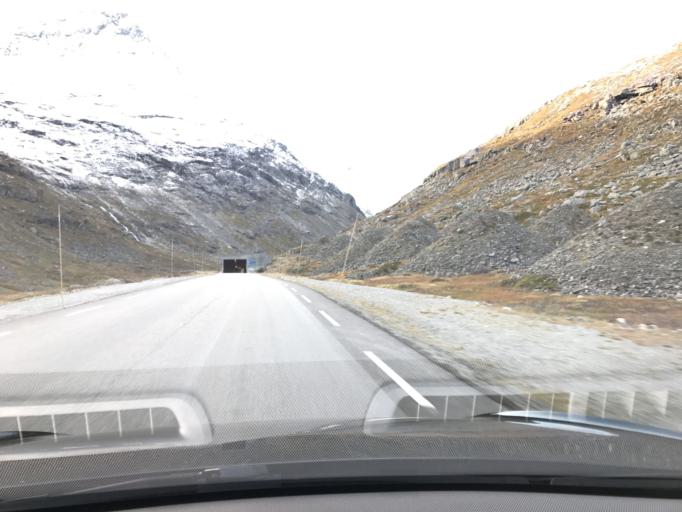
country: NO
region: More og Romsdal
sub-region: Norddal
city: Valldal
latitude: 61.9917
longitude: 7.3125
